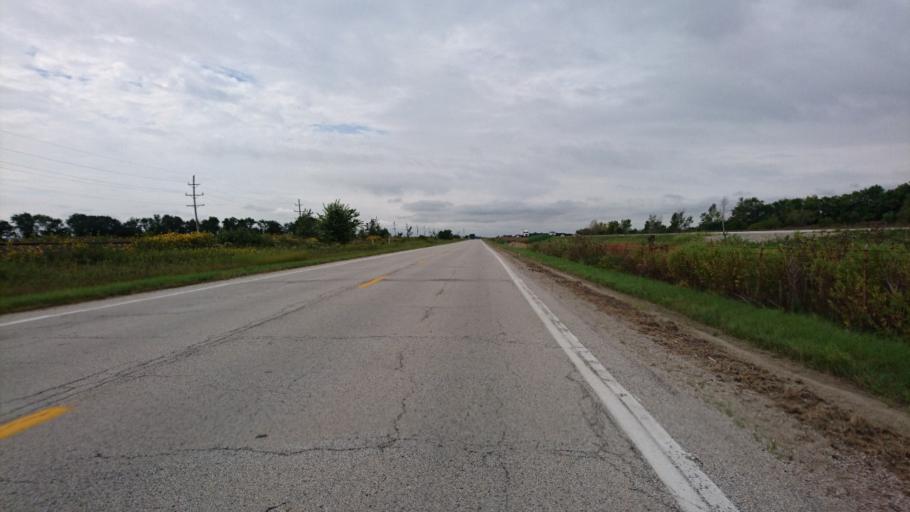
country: US
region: Illinois
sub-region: Livingston County
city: Dwight
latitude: 41.0637
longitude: -88.4646
